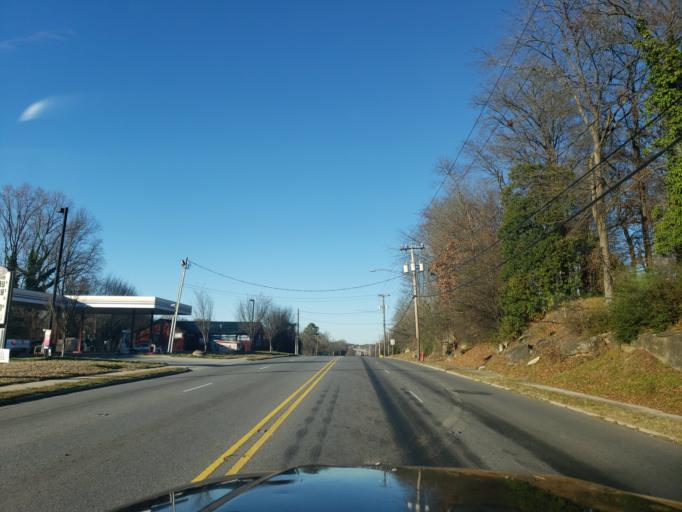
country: US
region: North Carolina
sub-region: Gaston County
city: Gastonia
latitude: 35.2699
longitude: -81.1878
